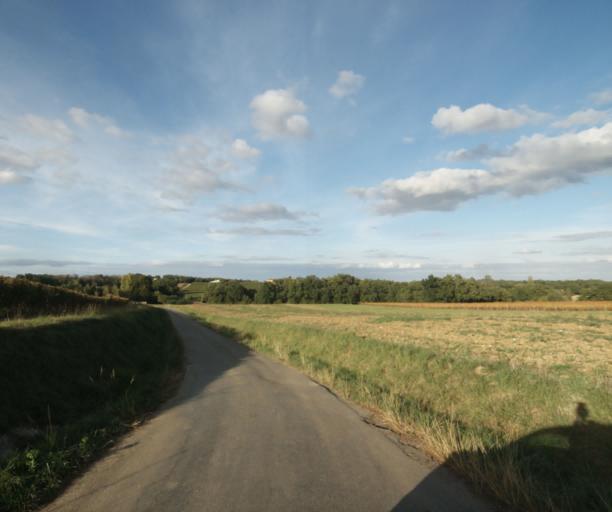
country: FR
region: Midi-Pyrenees
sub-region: Departement du Gers
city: Gondrin
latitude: 43.8855
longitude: 0.2446
